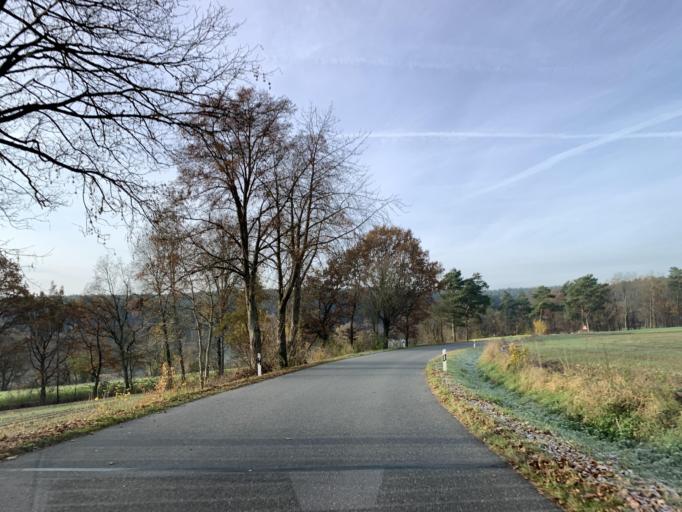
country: DE
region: Bavaria
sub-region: Upper Palatinate
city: Thanstein
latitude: 49.3488
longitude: 12.4409
